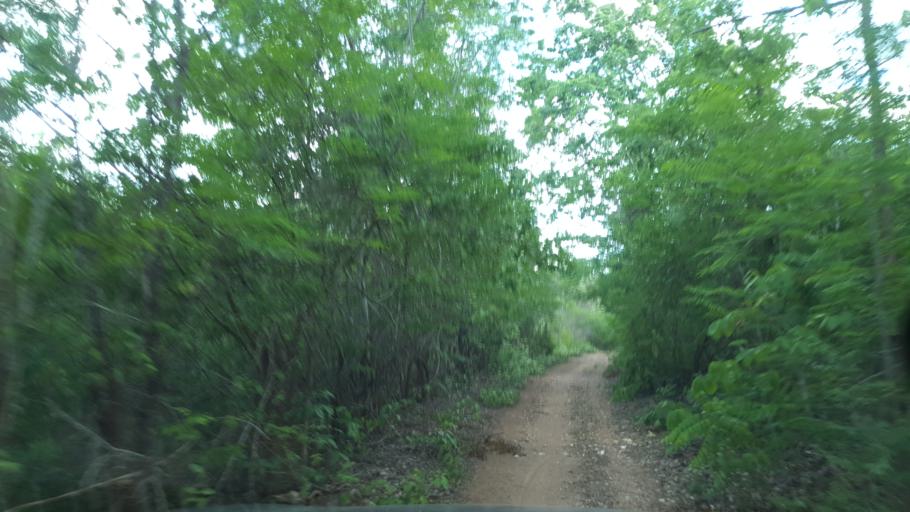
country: TH
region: Lampang
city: Sop Prap
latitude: 17.8896
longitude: 99.2876
